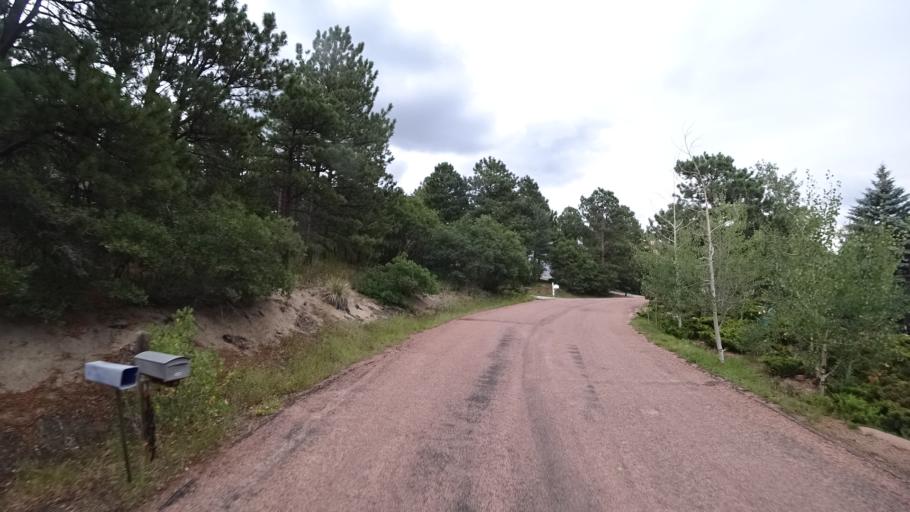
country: US
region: Colorado
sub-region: El Paso County
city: Woodmoor
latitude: 39.1023
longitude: -104.8545
